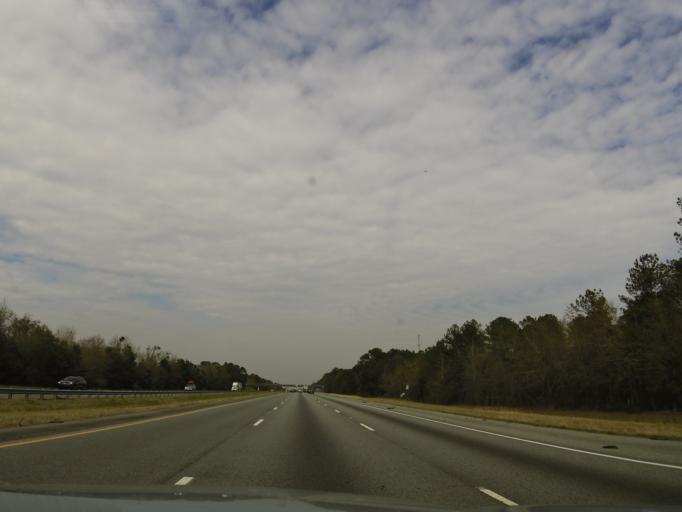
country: US
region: Georgia
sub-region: Liberty County
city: Midway
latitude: 31.6294
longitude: -81.4069
